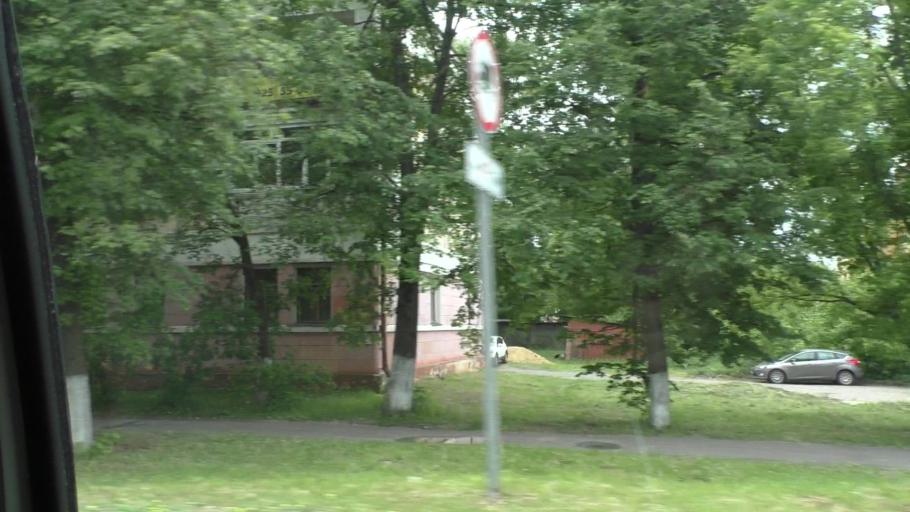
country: RU
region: Moskovskaya
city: Yegor'yevsk
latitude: 55.3923
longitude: 39.0219
